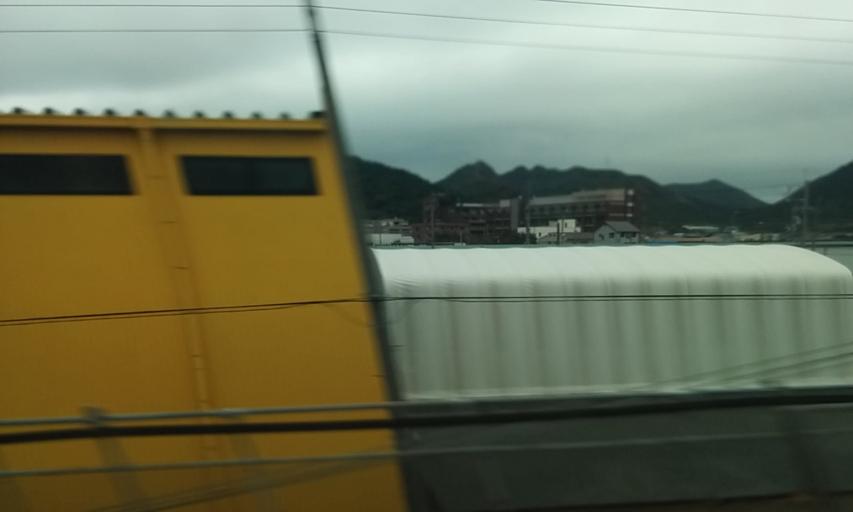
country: JP
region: Hyogo
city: Shirahamacho-usazakiminami
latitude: 34.8057
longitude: 134.7499
